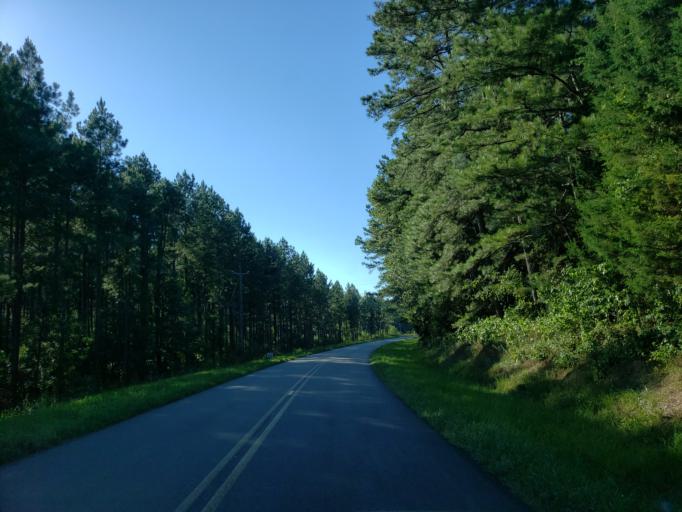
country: US
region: Georgia
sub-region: Bartow County
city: Euharlee
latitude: 34.1138
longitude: -85.0091
